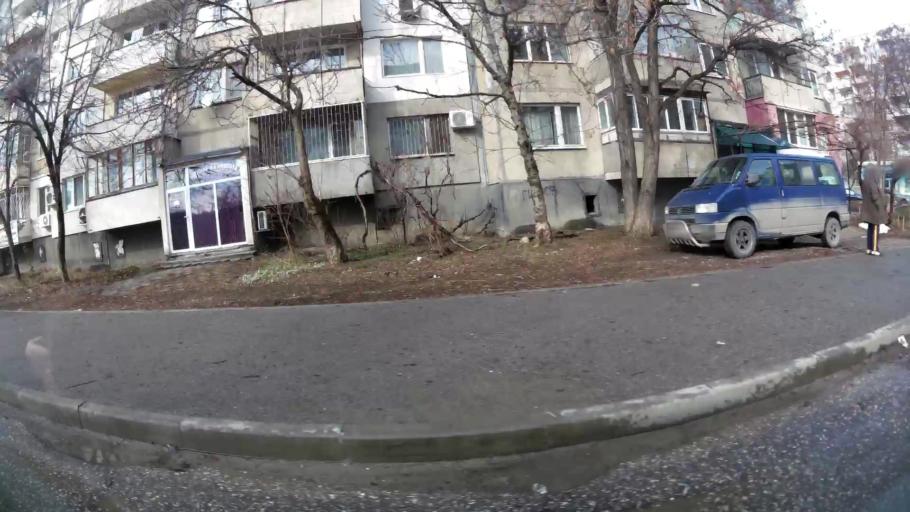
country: BG
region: Sofia-Capital
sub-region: Stolichna Obshtina
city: Sofia
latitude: 42.7157
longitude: 23.2752
